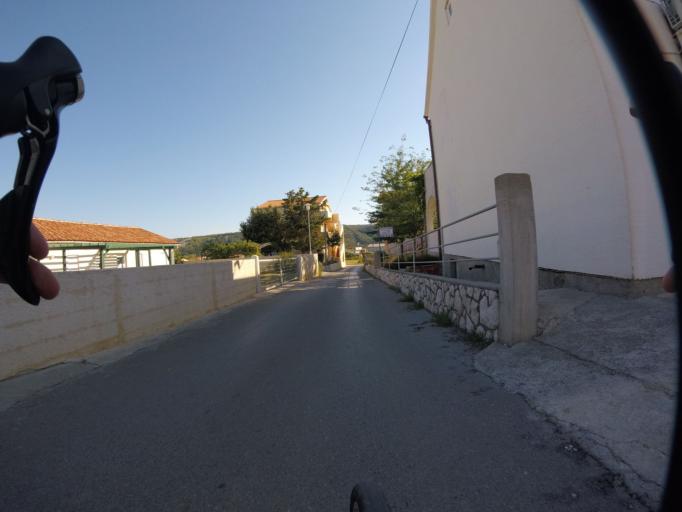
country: HR
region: Primorsko-Goranska
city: Lopar
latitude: 44.8330
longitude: 14.7337
